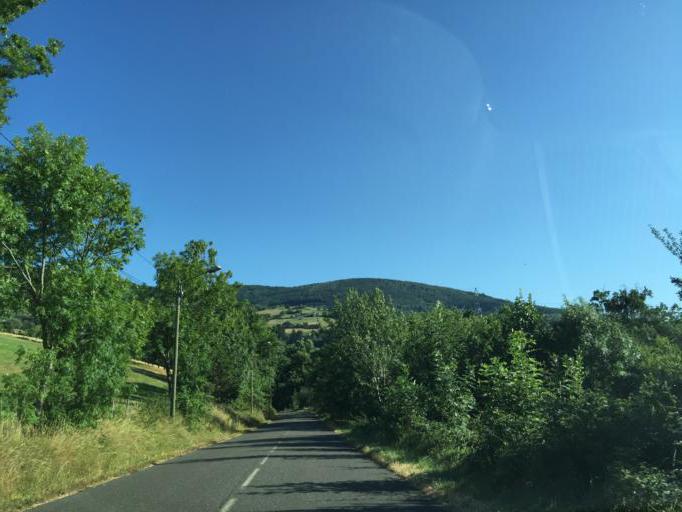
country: FR
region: Rhone-Alpes
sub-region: Departement de la Loire
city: Saint-Jean-Bonnefonds
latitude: 45.4478
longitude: 4.4807
